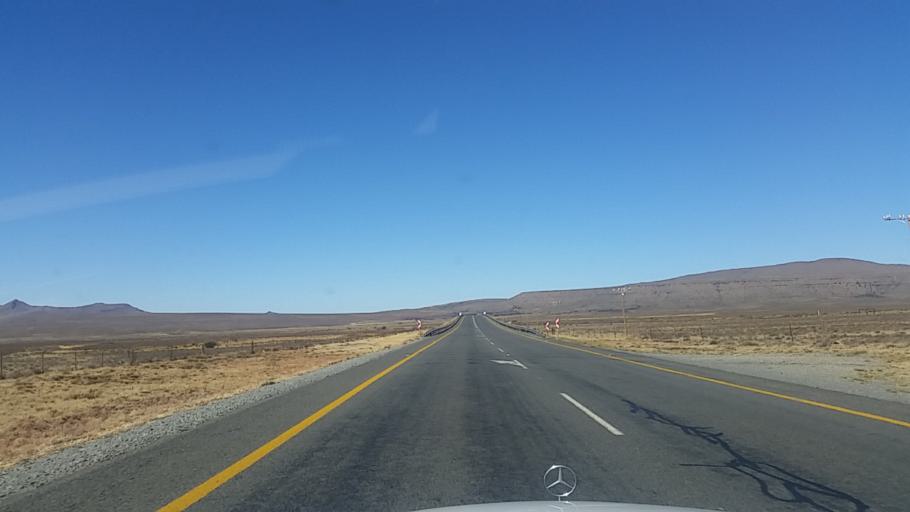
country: ZA
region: Eastern Cape
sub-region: Cacadu District Municipality
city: Graaff-Reinet
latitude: -31.9181
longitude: 24.7575
